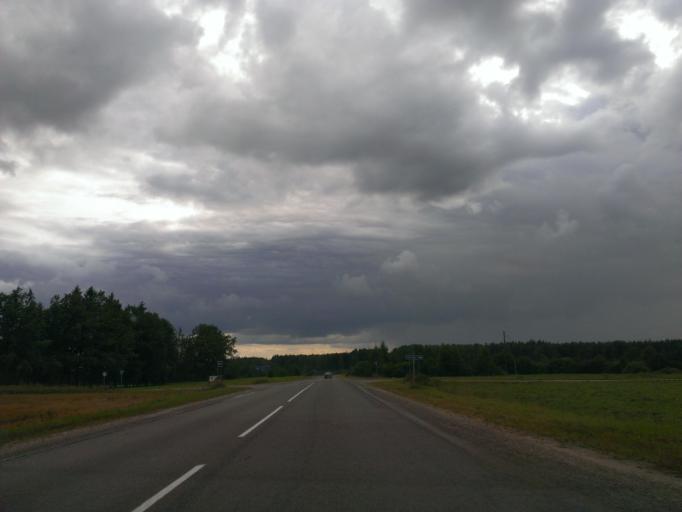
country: LV
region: Kegums
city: Kegums
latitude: 56.7709
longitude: 24.7717
